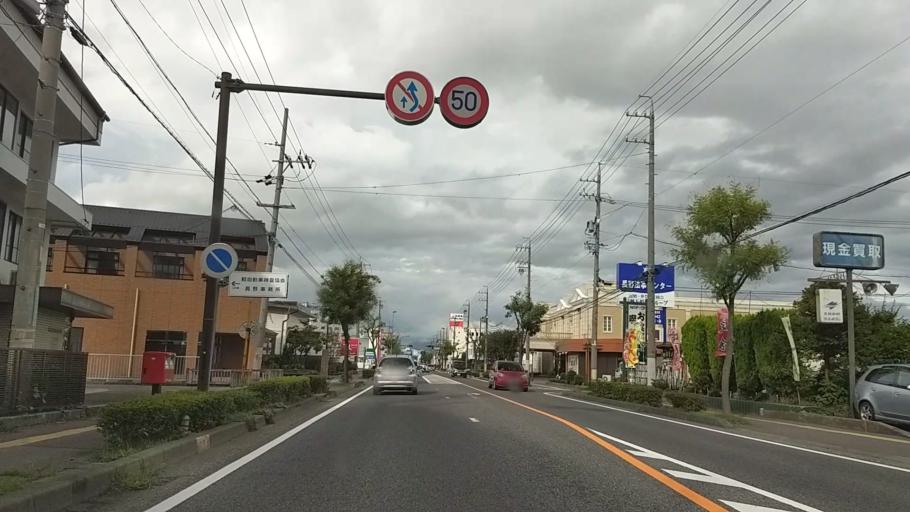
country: JP
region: Nagano
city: Nagano-shi
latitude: 36.6495
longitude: 138.2220
